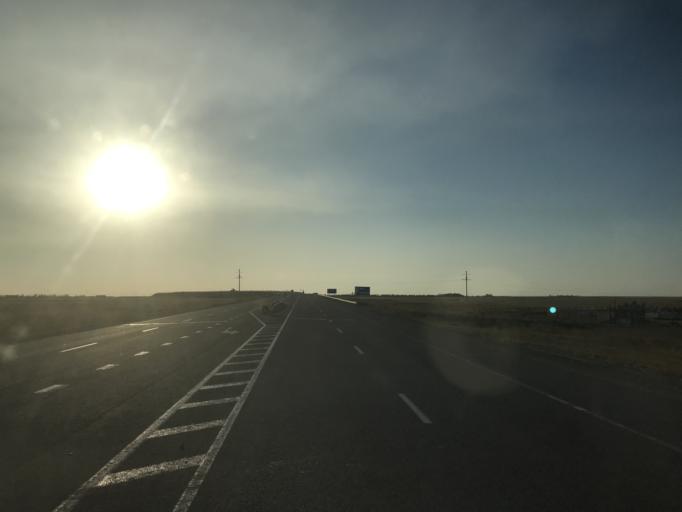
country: KZ
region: Pavlodar
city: Aksu
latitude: 52.1562
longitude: 76.8334
